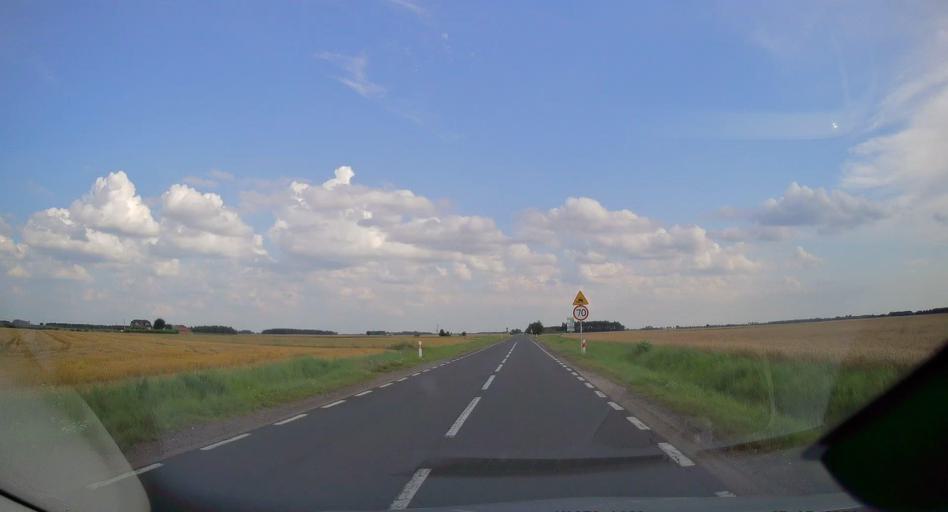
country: PL
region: Lodz Voivodeship
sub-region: Powiat tomaszowski
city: Rzeczyca
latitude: 51.6677
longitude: 20.2636
